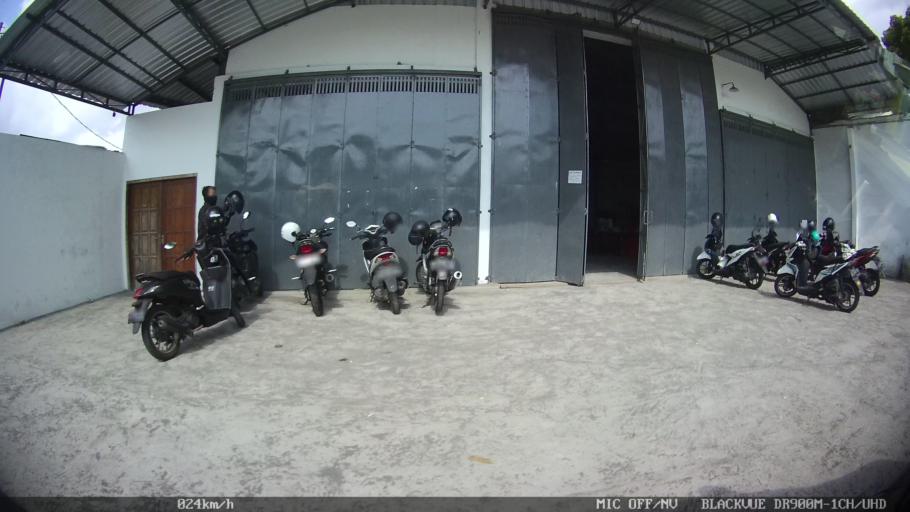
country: ID
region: Daerah Istimewa Yogyakarta
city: Kasihan
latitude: -7.8364
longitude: 110.3126
